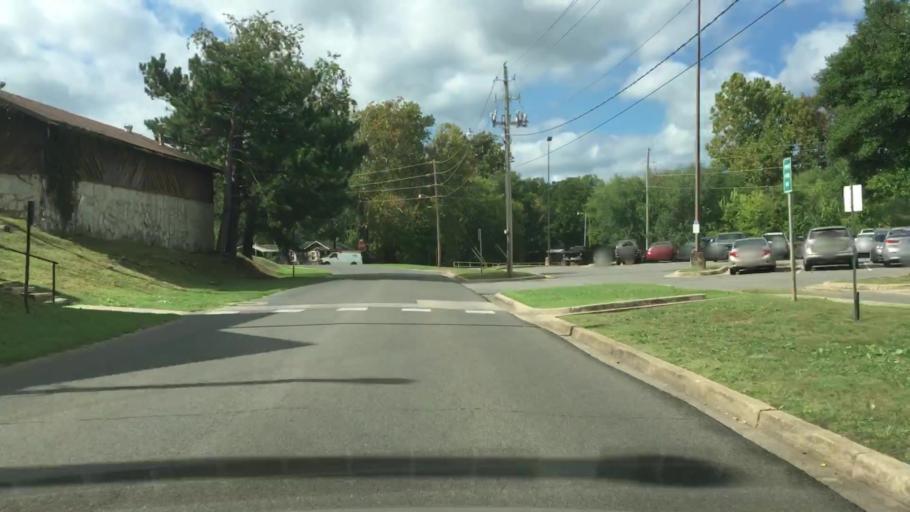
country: US
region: Oklahoma
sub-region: Cherokee County
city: Tahlequah
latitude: 35.9215
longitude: -94.9705
